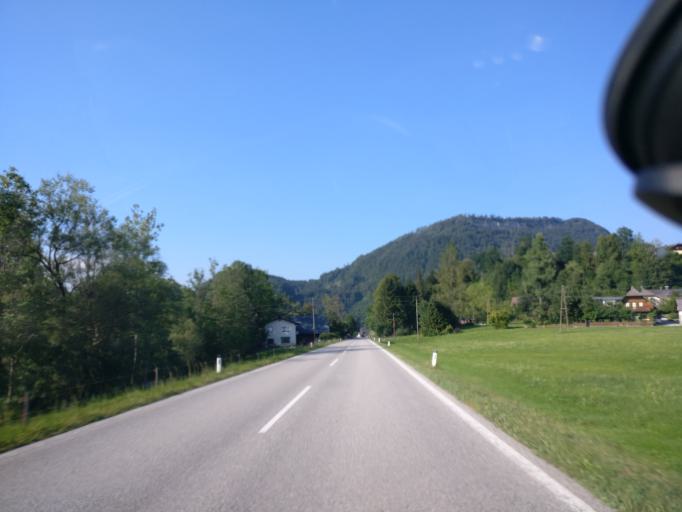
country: AT
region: Lower Austria
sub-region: Politischer Bezirk Scheibbs
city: Gostling an der Ybbs
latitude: 47.8007
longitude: 14.9287
